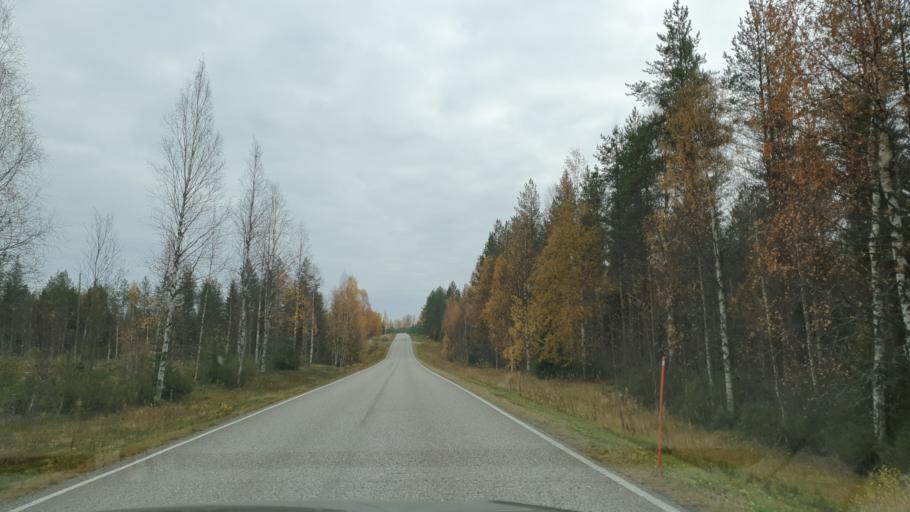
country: FI
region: Kainuu
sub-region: Kajaani
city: Ristijaervi
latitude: 64.6094
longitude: 27.9991
